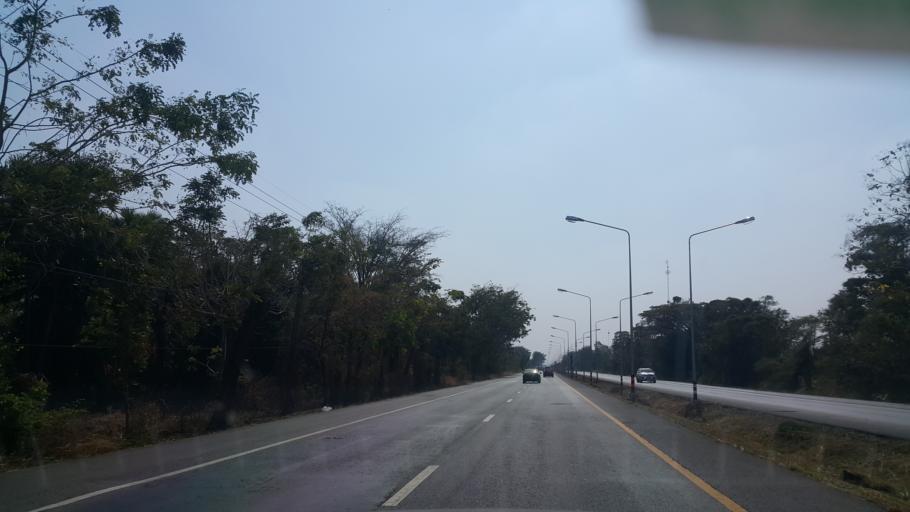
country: TH
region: Nakhon Ratchasima
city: Non Daeng
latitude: 15.3657
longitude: 102.4549
